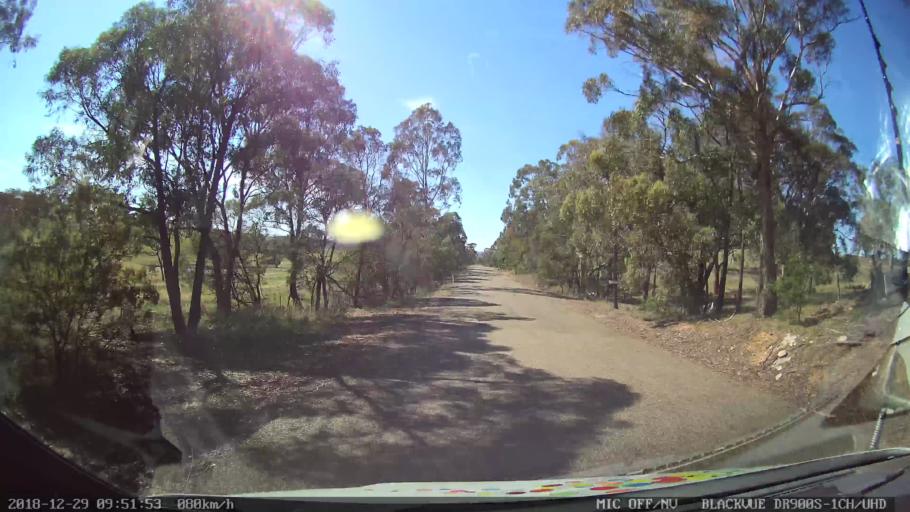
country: AU
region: New South Wales
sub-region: Goulburn Mulwaree
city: Goulburn
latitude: -34.7371
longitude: 149.4624
